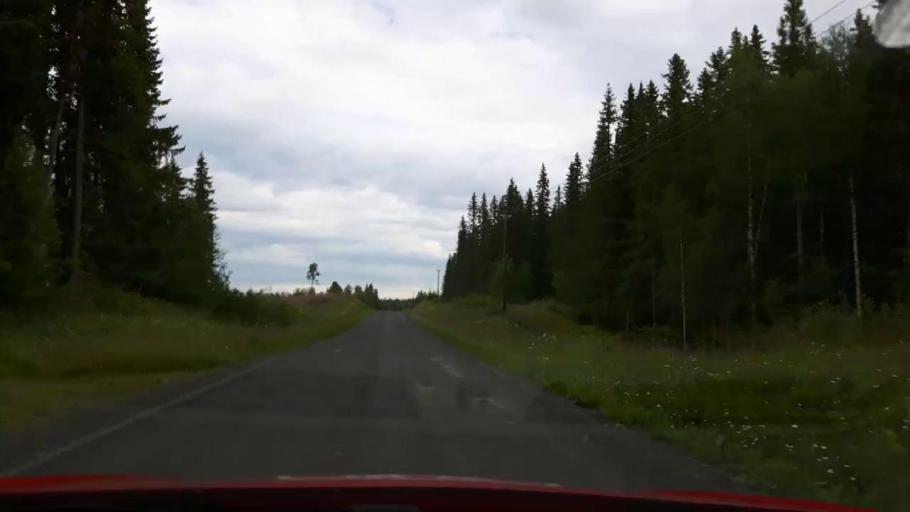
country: SE
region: Jaemtland
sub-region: Stroemsunds Kommun
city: Stroemsund
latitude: 63.4836
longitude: 15.3055
